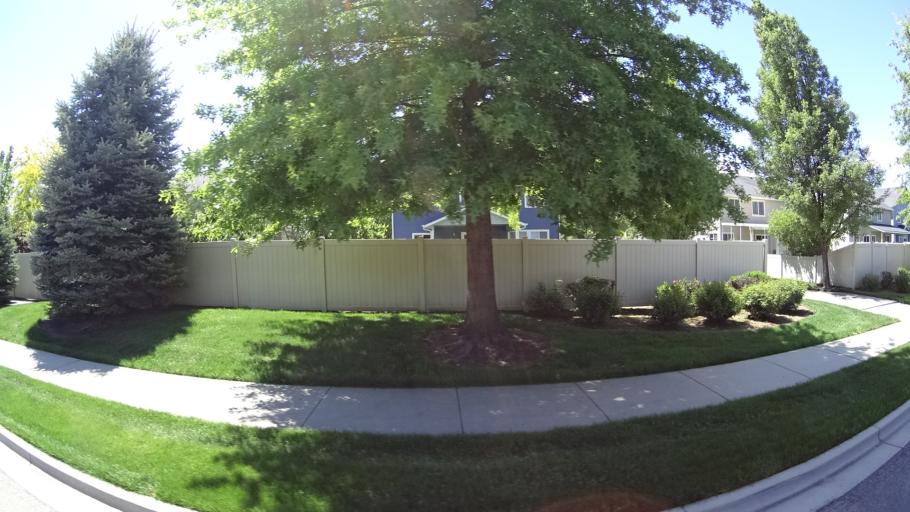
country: US
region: Idaho
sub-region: Ada County
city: Meridian
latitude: 43.6285
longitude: -116.3377
